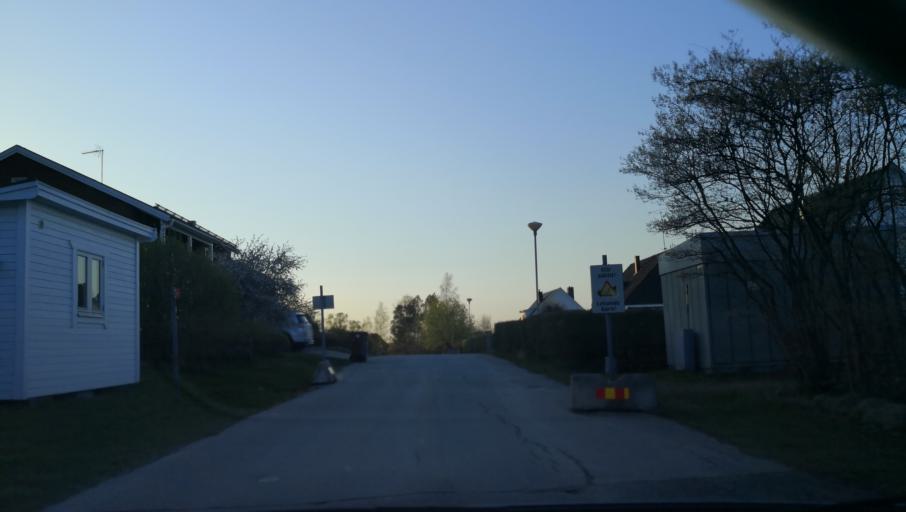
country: SE
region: Stockholm
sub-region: Varmdo Kommun
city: Mortnas
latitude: 59.3200
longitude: 18.4720
